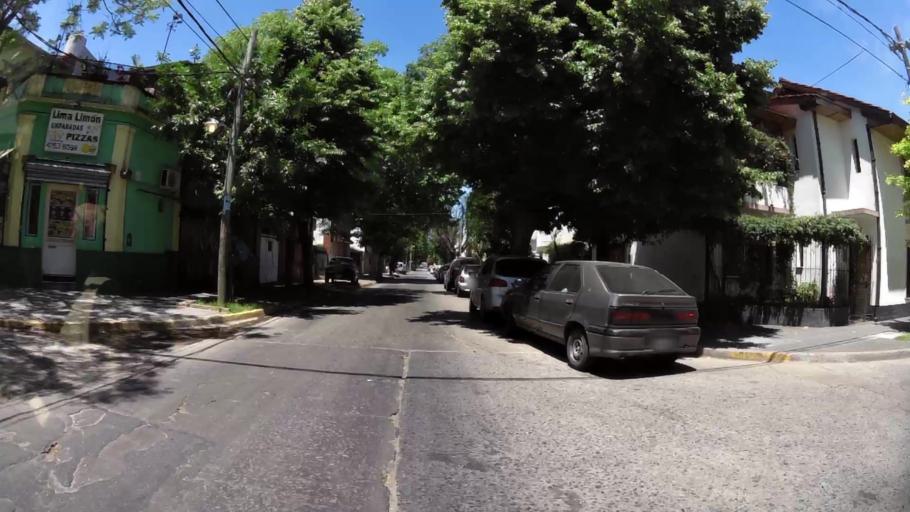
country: AR
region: Buenos Aires
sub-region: Partido de General San Martin
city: General San Martin
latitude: -34.5819
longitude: -58.5424
